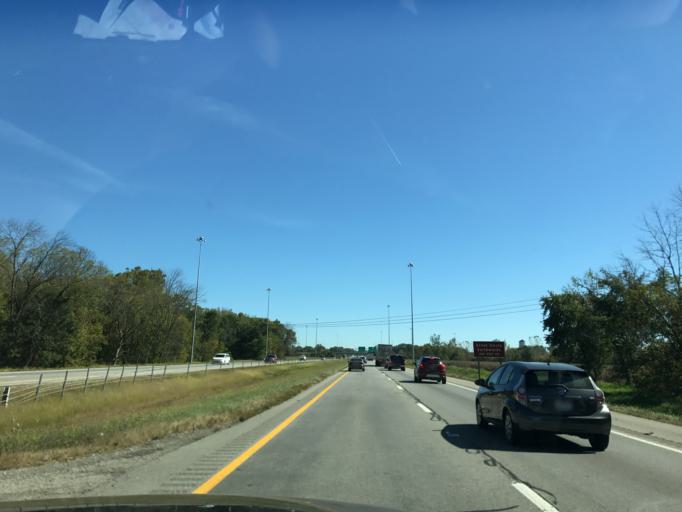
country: US
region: Ohio
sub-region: Licking County
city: Hebron
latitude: 39.9443
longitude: -82.4906
